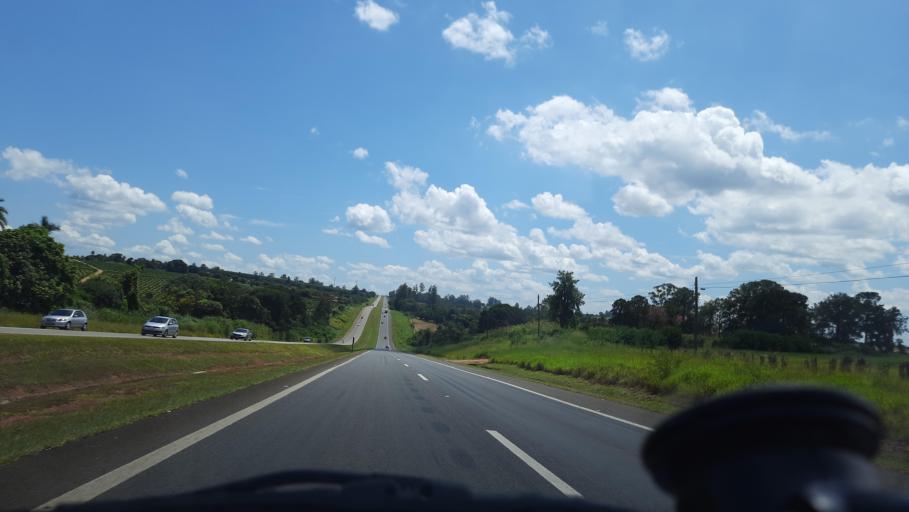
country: BR
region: Sao Paulo
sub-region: Moji-Guacu
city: Mogi-Gaucu
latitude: -22.2511
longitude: -46.9775
